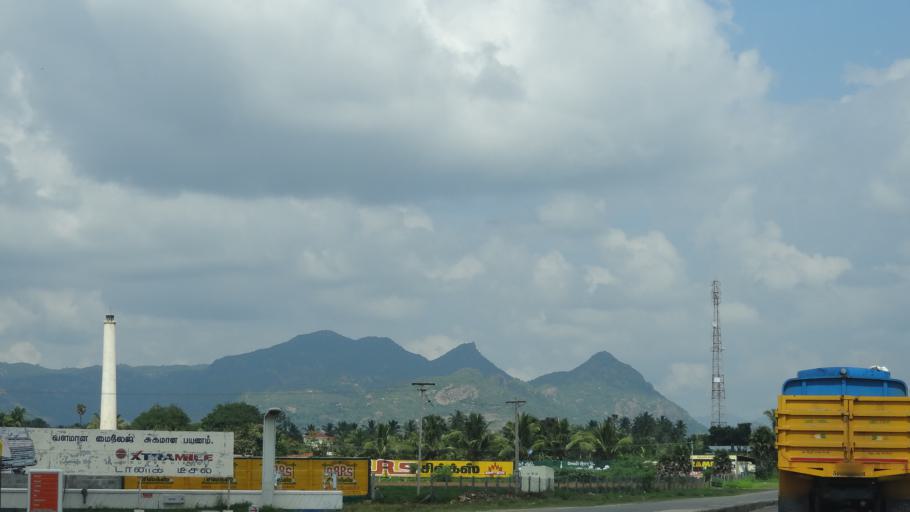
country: IN
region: Tamil Nadu
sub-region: Salem
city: Omalur
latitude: 11.8568
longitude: 78.0742
